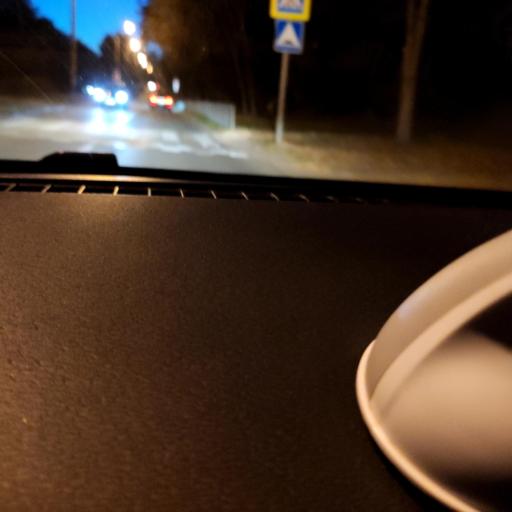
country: RU
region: Samara
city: Samara
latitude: 53.2279
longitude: 50.2177
